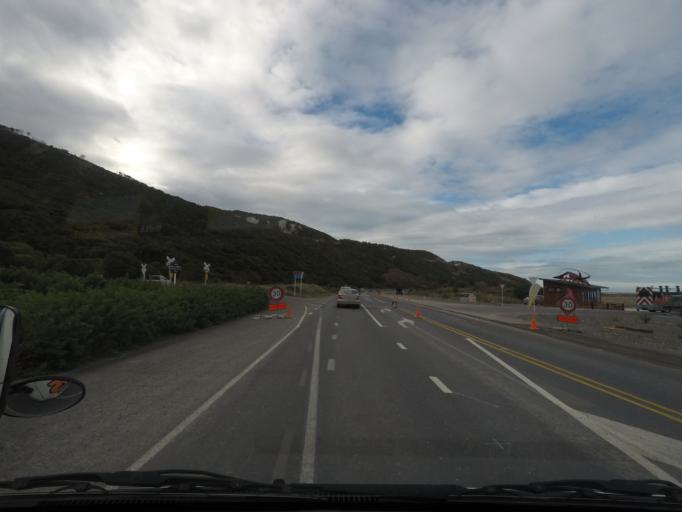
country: NZ
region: Canterbury
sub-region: Kaikoura District
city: Kaikoura
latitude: -42.2174
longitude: 173.8594
